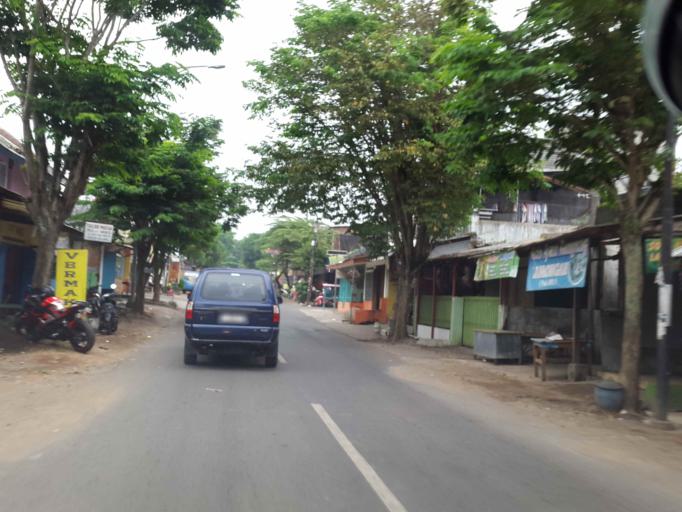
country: ID
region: East Java
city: Niwen
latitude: -7.9878
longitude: 112.5980
